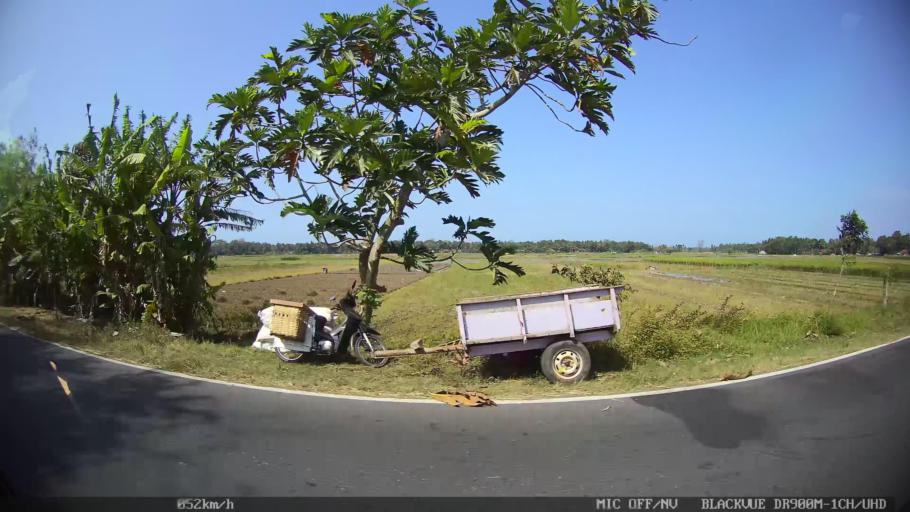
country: ID
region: Daerah Istimewa Yogyakarta
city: Srandakan
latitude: -7.9331
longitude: 110.2156
